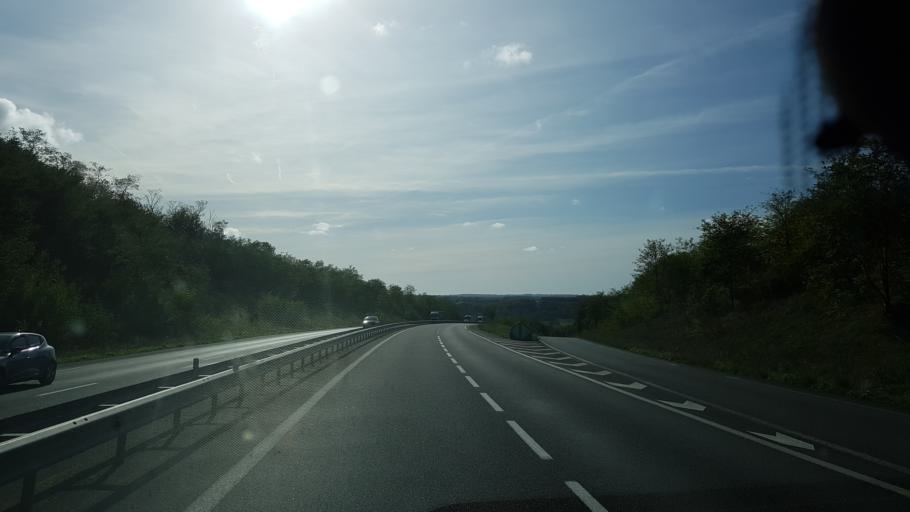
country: FR
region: Poitou-Charentes
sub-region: Departement de la Charente
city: La Rochefoucauld
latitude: 45.7574
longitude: 0.3908
